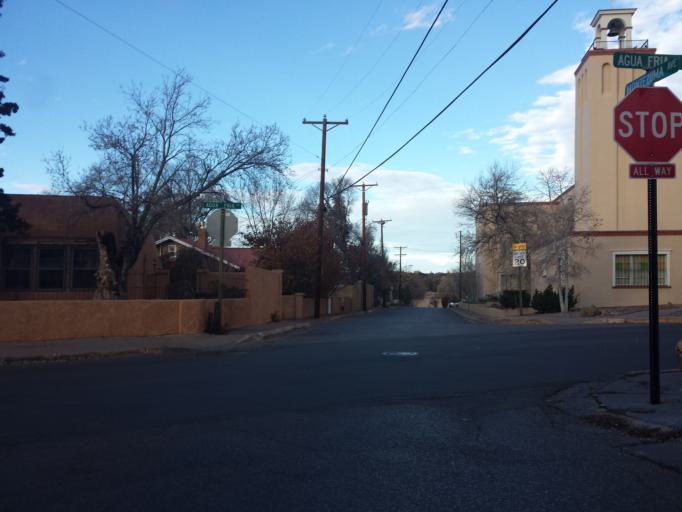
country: US
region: New Mexico
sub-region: Santa Fe County
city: Santa Fe
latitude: 35.6865
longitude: -105.9463
